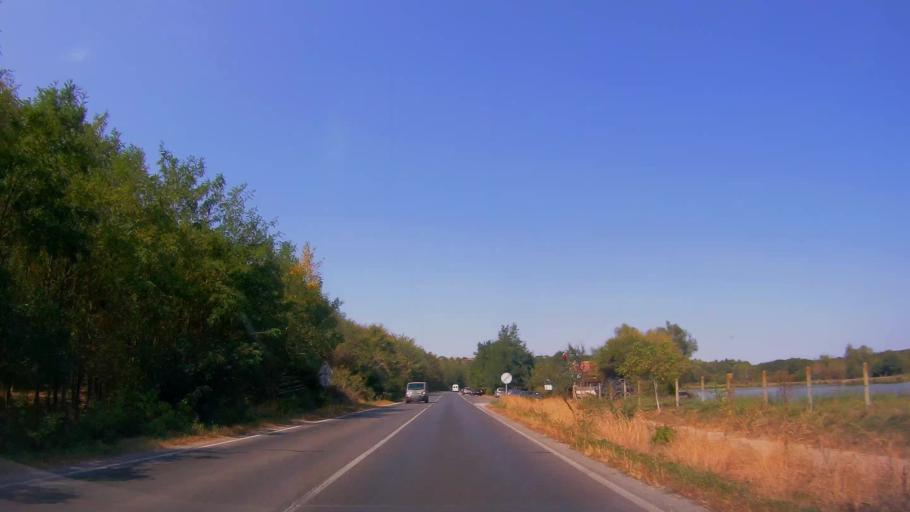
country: BG
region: Razgrad
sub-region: Obshtina Tsar Kaloyan
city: Tsar Kaloyan
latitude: 43.6168
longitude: 26.2138
